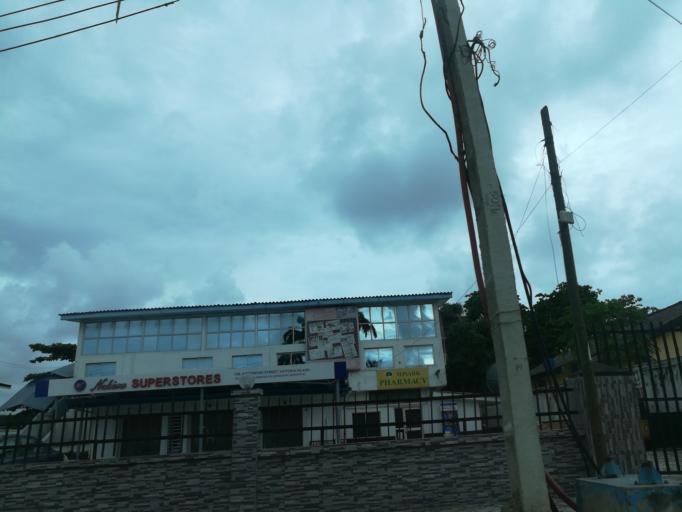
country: NG
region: Lagos
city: Ikoyi
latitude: 6.4316
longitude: 3.4152
